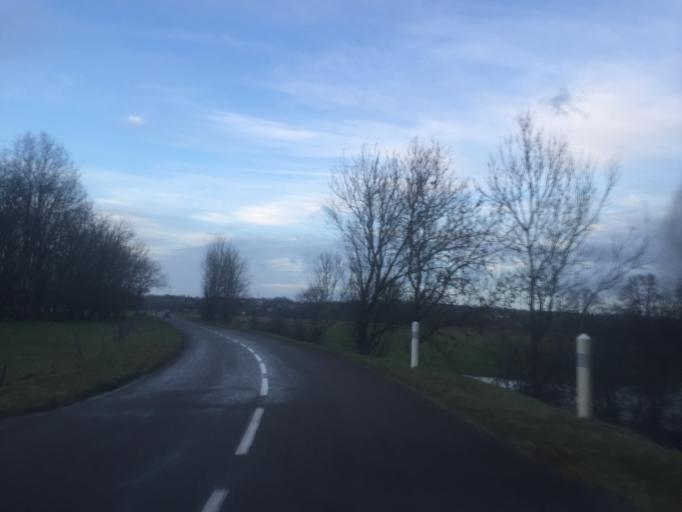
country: FR
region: Franche-Comte
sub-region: Departement du Jura
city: Orchamps
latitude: 47.1361
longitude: 5.6591
